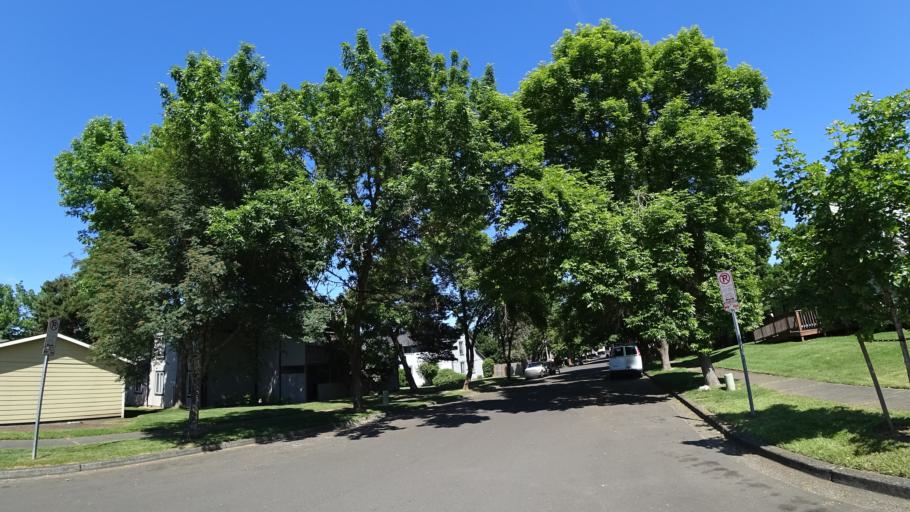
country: US
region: Oregon
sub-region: Washington County
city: Beaverton
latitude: 45.4500
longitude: -122.8044
